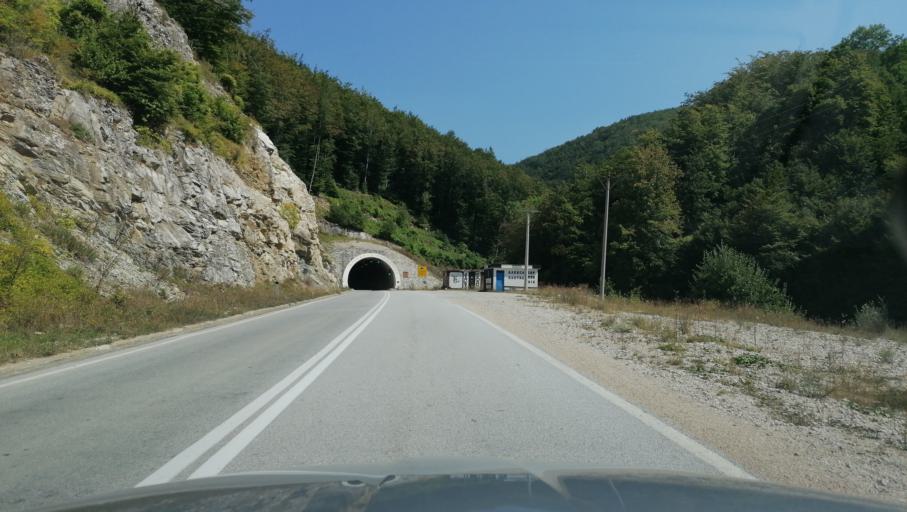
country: BA
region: Republika Srpska
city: Gacko
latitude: 43.2325
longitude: 18.5927
